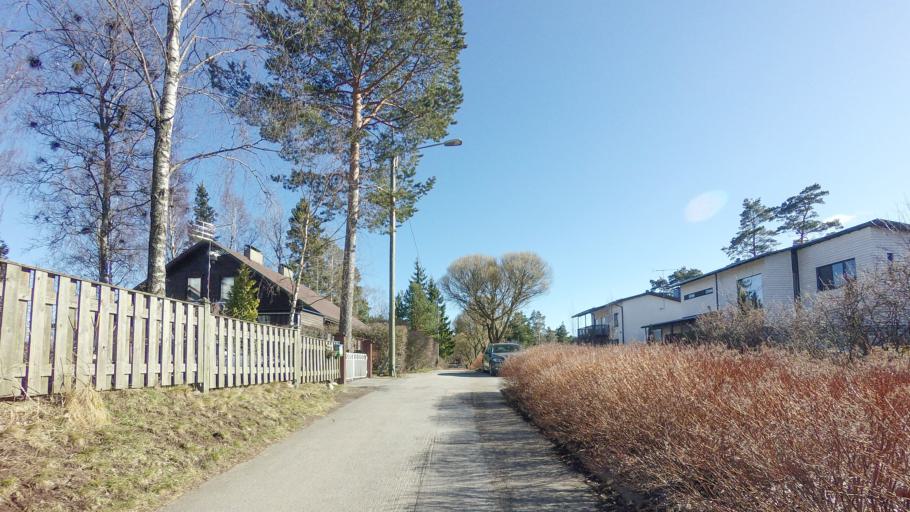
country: FI
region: Uusimaa
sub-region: Helsinki
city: Helsinki
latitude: 60.1626
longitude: 25.0633
